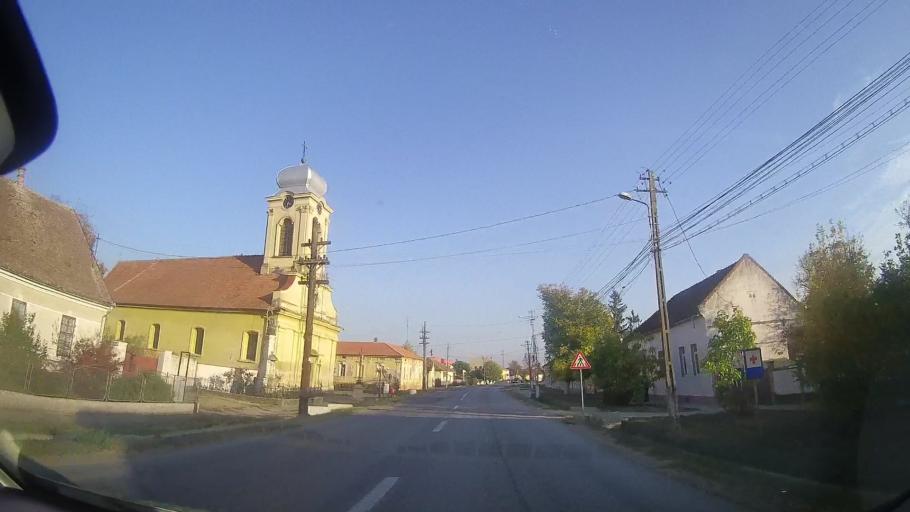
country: RO
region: Timis
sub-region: Comuna Pischia
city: Pischia
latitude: 45.9019
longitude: 21.3401
